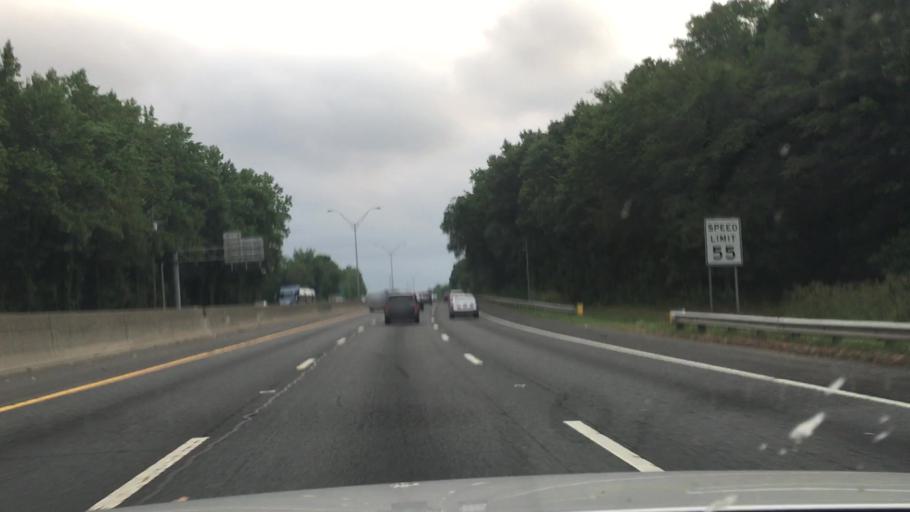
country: US
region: North Carolina
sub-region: Mecklenburg County
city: Charlotte
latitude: 35.2039
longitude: -80.8795
